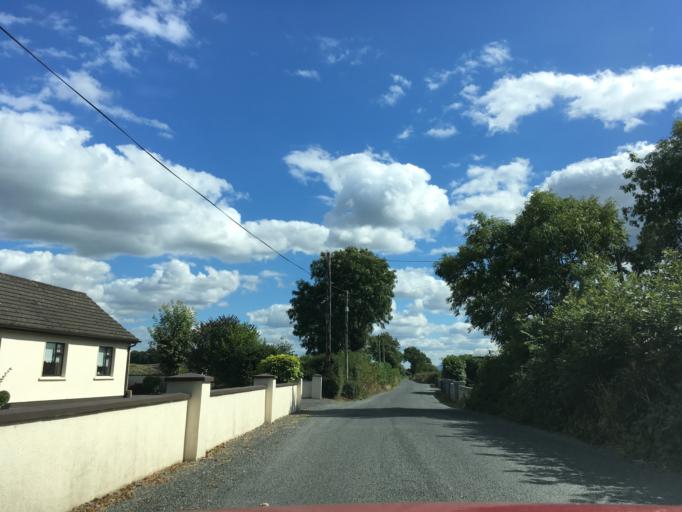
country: IE
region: Munster
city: Cashel
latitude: 52.4723
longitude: -7.9795
